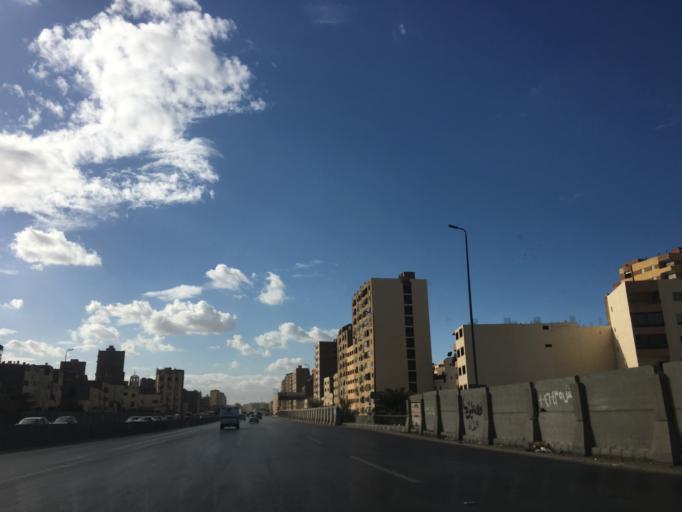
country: EG
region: Al Jizah
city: Al Jizah
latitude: 30.0132
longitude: 31.1590
